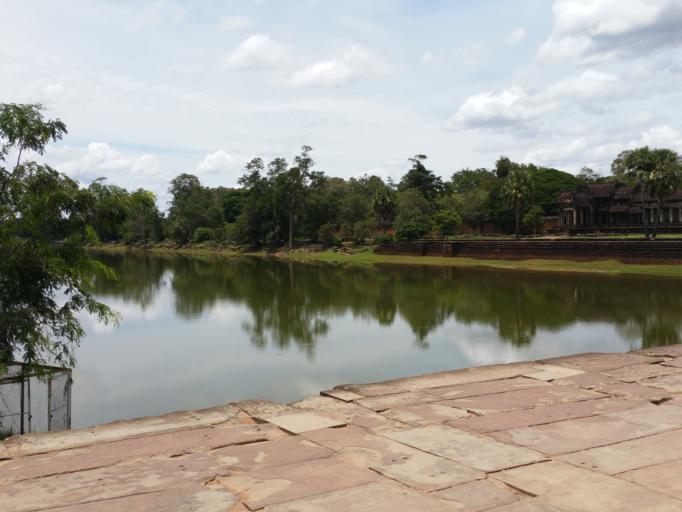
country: KH
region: Siem Reap
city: Siem Reap
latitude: 13.4125
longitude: 103.8606
